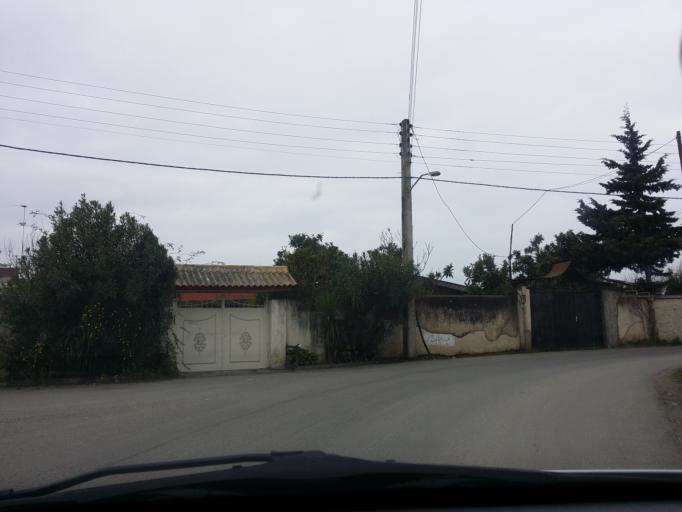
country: IR
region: Mazandaran
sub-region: Nowshahr
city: Nowshahr
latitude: 36.6562
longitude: 51.4769
